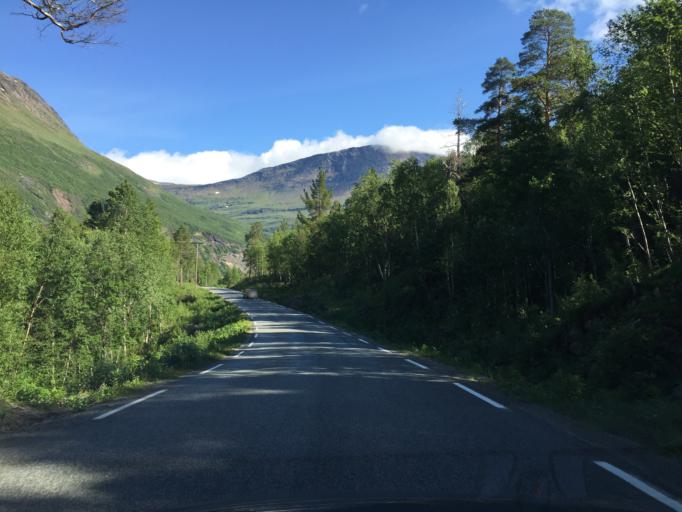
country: NO
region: Nordland
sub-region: Saltdal
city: Rognan
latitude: 66.8165
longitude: 15.4608
